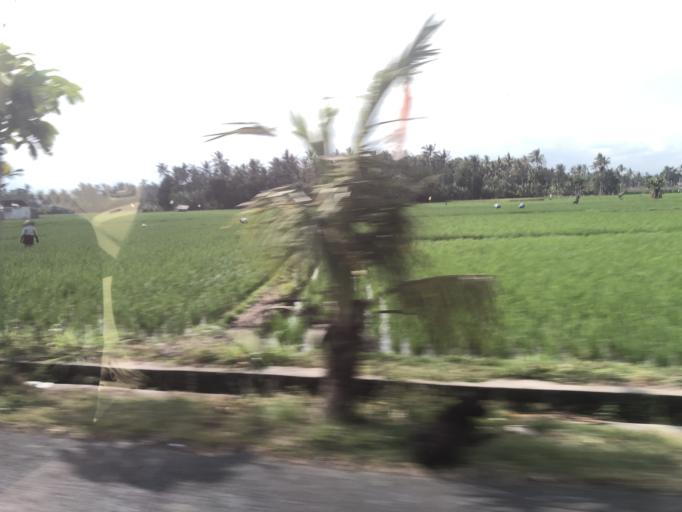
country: ID
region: Bali
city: Banjar Bucu
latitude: -8.5776
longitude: 115.2016
